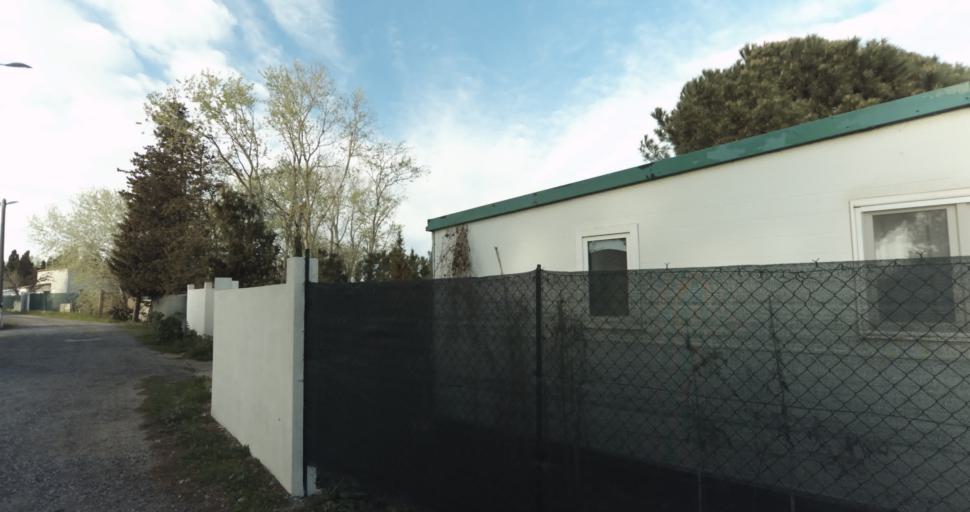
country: FR
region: Languedoc-Roussillon
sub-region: Departement de l'Herault
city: Marseillan
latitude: 43.3172
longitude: 3.5372
